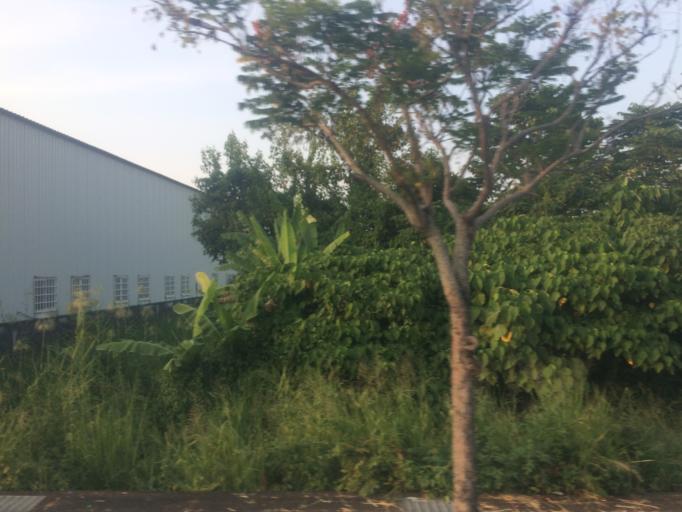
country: TW
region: Taiwan
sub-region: Chiayi
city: Jiayi Shi
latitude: 23.5501
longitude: 120.4267
